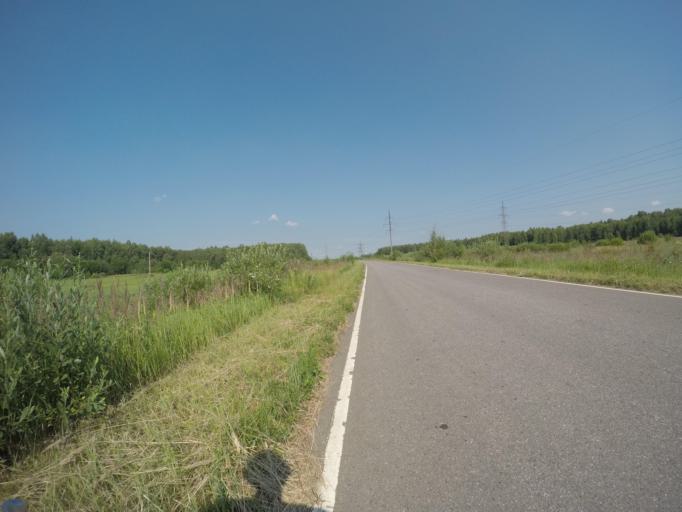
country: RU
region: Moskovskaya
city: Rechitsy
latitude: 55.6242
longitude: 38.5227
